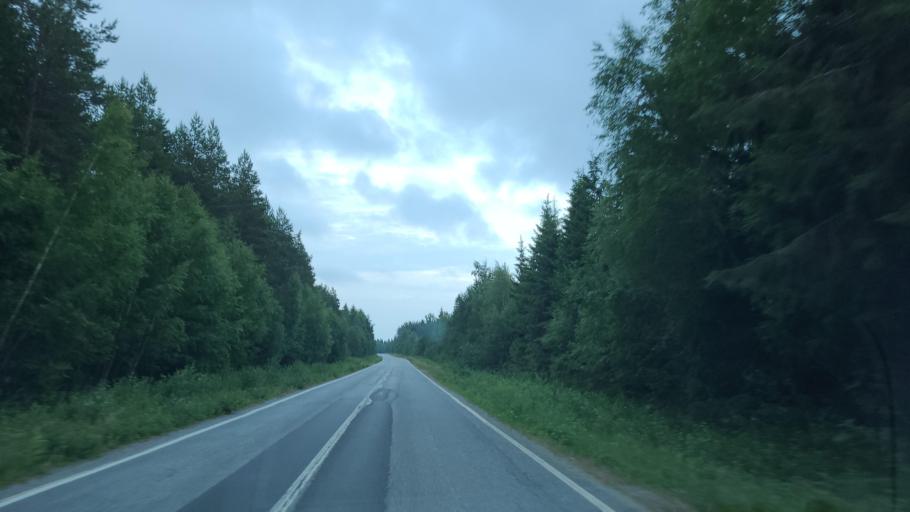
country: FI
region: Ostrobothnia
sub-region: Vaasa
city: Replot
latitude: 63.2735
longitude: 21.1439
